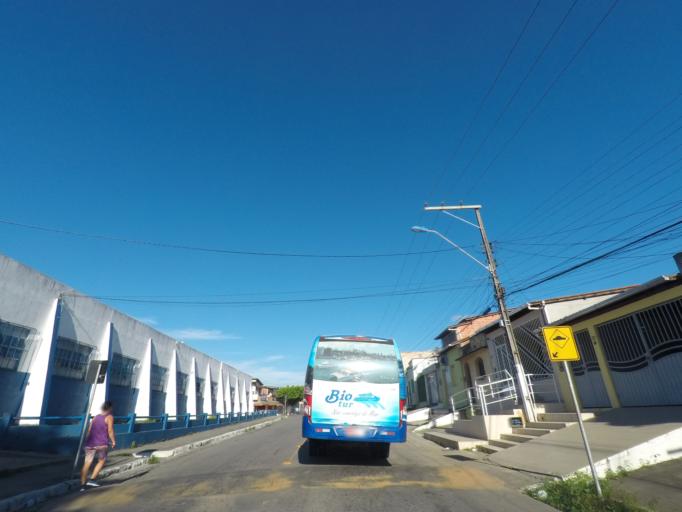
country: BR
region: Bahia
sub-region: Nazare
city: Nazare
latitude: -13.0348
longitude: -39.0160
